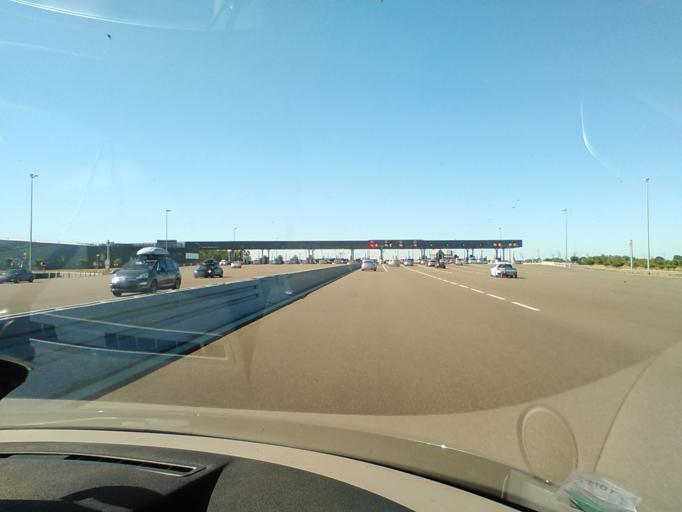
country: FR
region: Aquitaine
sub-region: Departement des Landes
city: Pissos
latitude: 44.3484
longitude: -0.8594
